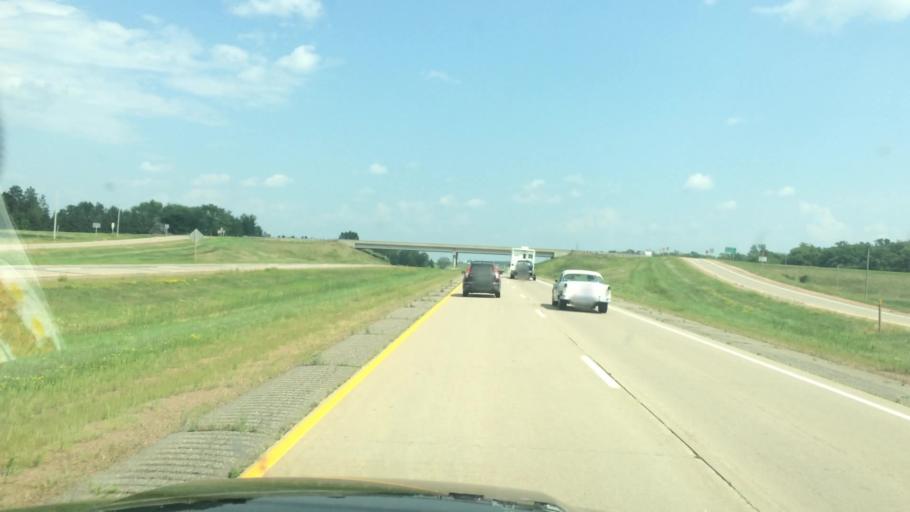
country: US
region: Wisconsin
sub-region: Marathon County
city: Athens
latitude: 44.9453
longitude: -90.0829
